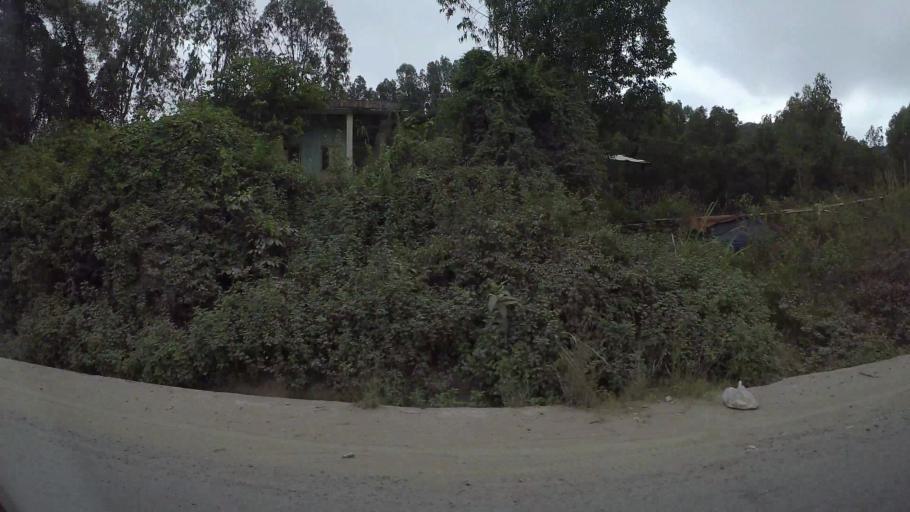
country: VN
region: Da Nang
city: Lien Chieu
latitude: 16.0392
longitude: 108.1714
